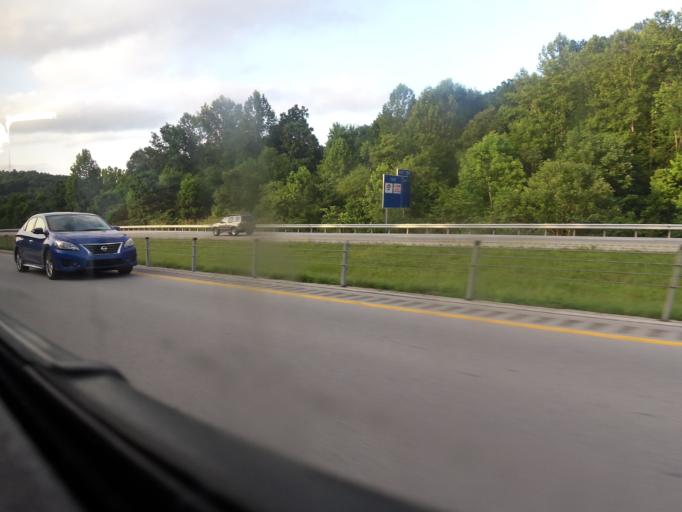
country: US
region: Kentucky
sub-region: Rockcastle County
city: Mount Vernon
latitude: 37.3335
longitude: -84.3047
